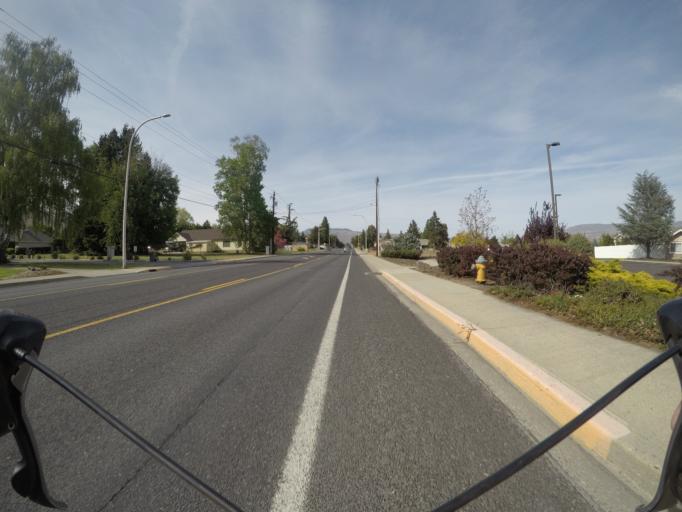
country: US
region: Washington
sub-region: Chelan County
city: West Wenatchee
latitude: 47.4251
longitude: -120.3459
